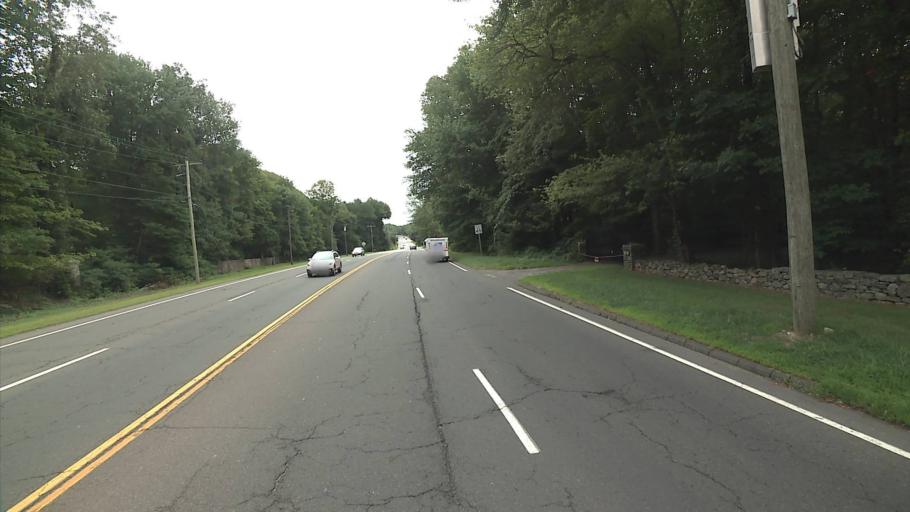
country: US
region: Connecticut
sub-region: Middlesex County
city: Old Saybrook Center
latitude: 41.3192
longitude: -72.3386
